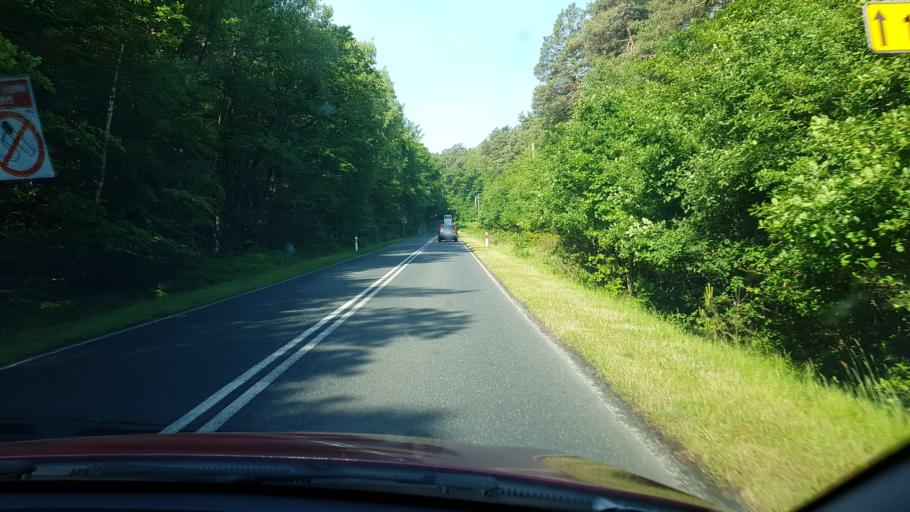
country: PL
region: West Pomeranian Voivodeship
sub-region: Powiat kamienski
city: Miedzyzdroje
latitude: 53.9657
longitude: 14.5481
